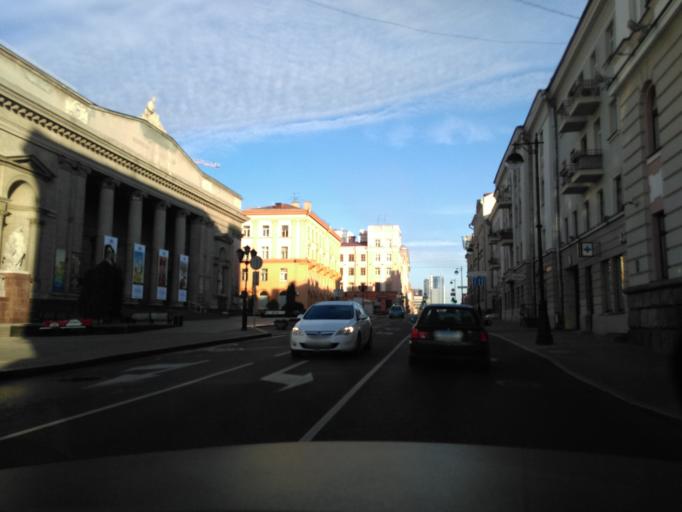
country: BY
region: Minsk
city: Minsk
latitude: 53.8983
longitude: 27.5618
